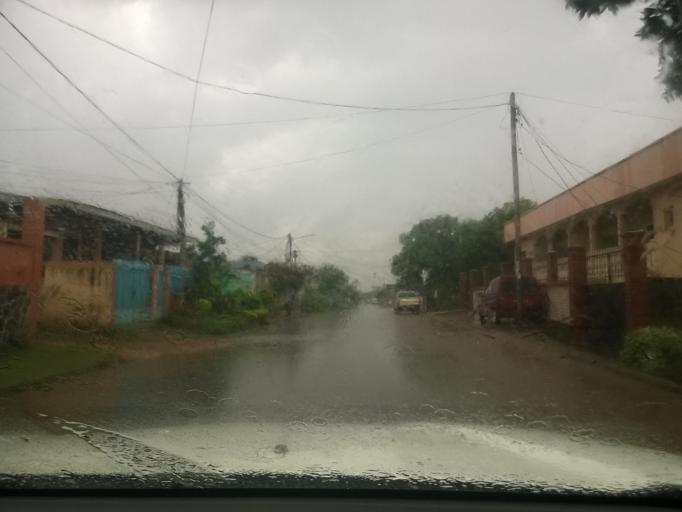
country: CM
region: Centre
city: Yaounde
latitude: 3.8732
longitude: 11.5358
